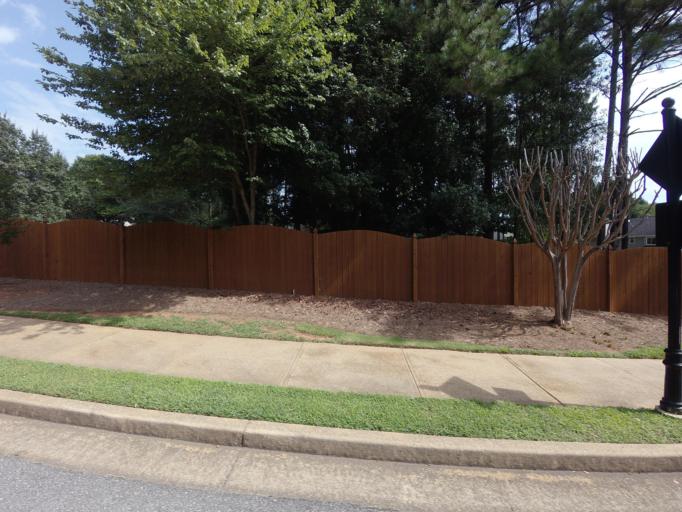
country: US
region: Georgia
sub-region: Fulton County
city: Johns Creek
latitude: 34.0457
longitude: -84.2357
